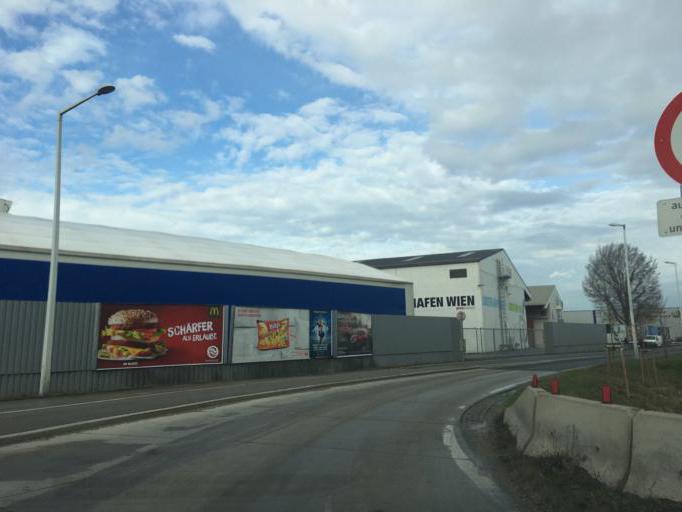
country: AT
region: Lower Austria
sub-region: Politischer Bezirk Wien-Umgebung
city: Schwechat
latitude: 48.1752
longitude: 16.4779
